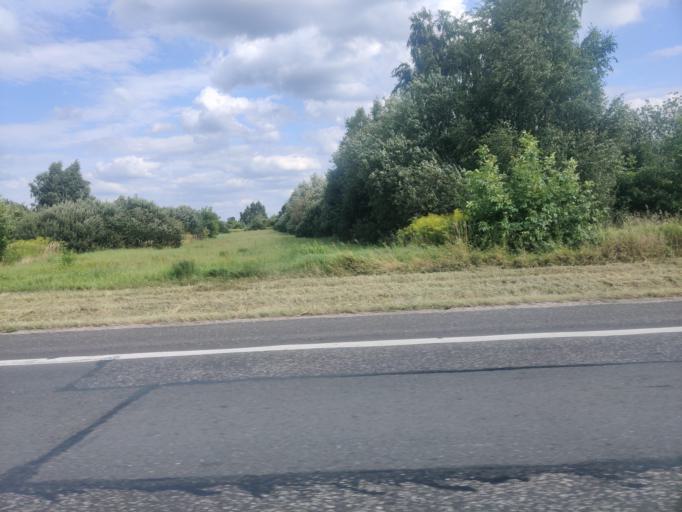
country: PL
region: Greater Poland Voivodeship
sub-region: Konin
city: Konin
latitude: 52.1972
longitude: 18.2684
